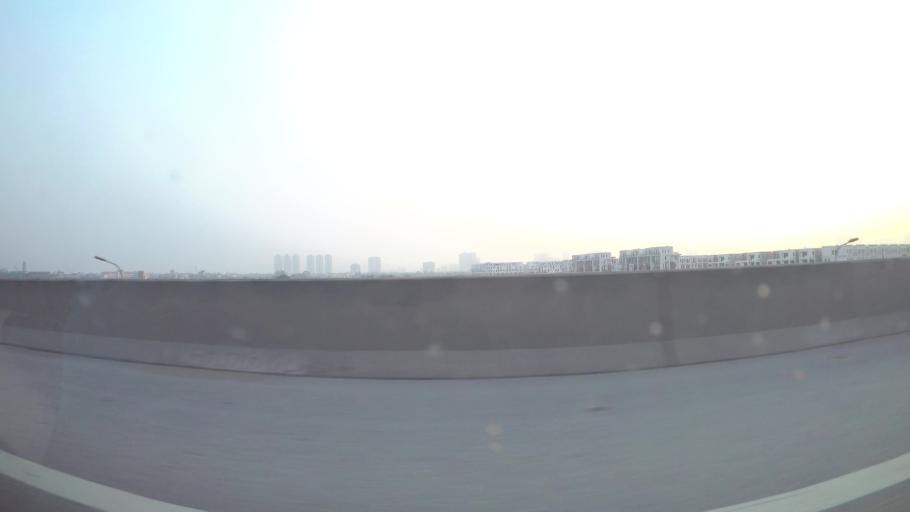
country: VN
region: Ha Noi
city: Thanh Xuan
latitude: 20.9745
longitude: 105.8160
